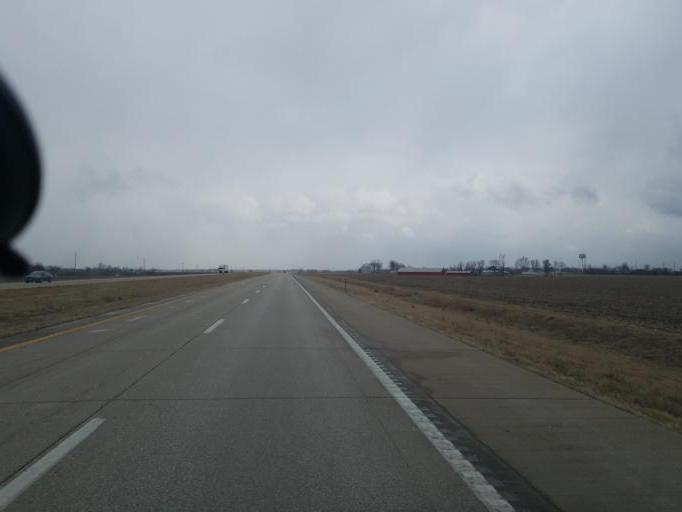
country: US
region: Missouri
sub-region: Randolph County
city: Moberly
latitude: 39.5277
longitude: -92.4422
